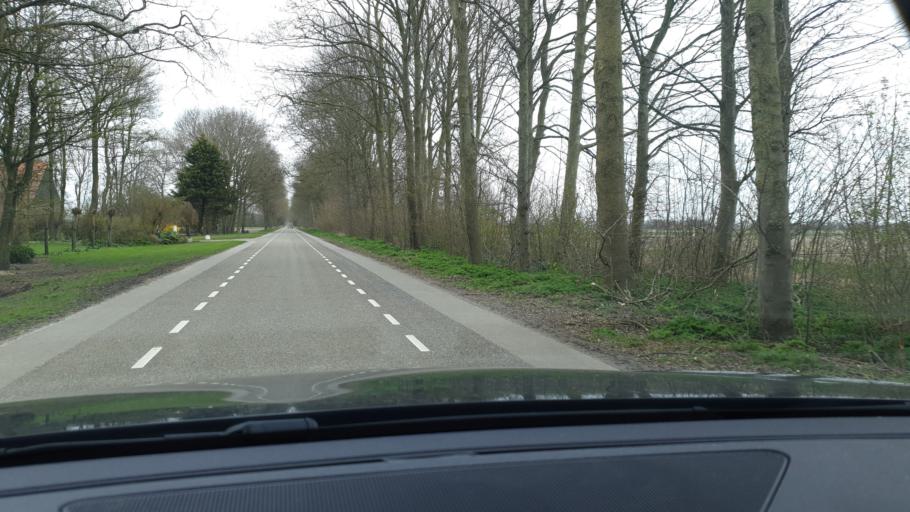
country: NL
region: Friesland
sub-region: Gemeente Lemsterland
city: Lemmer
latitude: 52.7814
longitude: 5.6279
